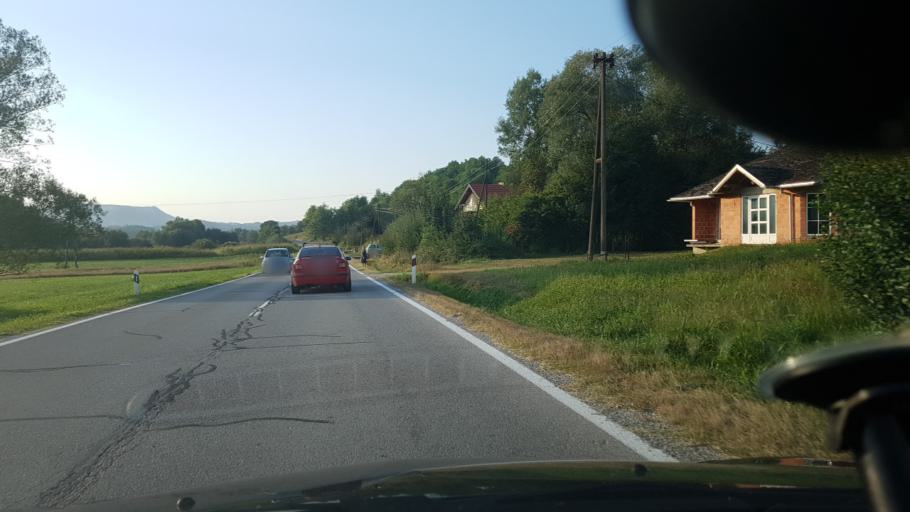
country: HR
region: Krapinsko-Zagorska
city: Pregrada
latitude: 46.1290
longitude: 15.8003
